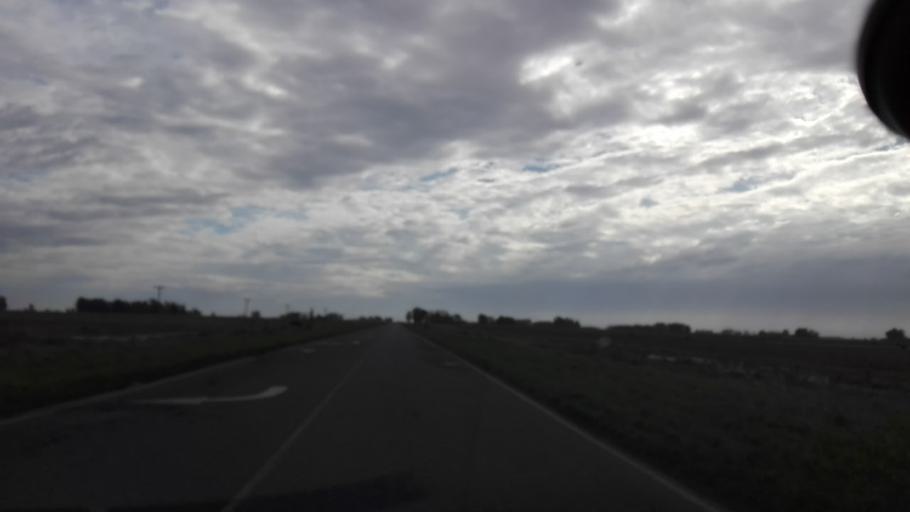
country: AR
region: Buenos Aires
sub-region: Partido de Las Flores
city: Las Flores
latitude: -36.1744
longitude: -59.0633
